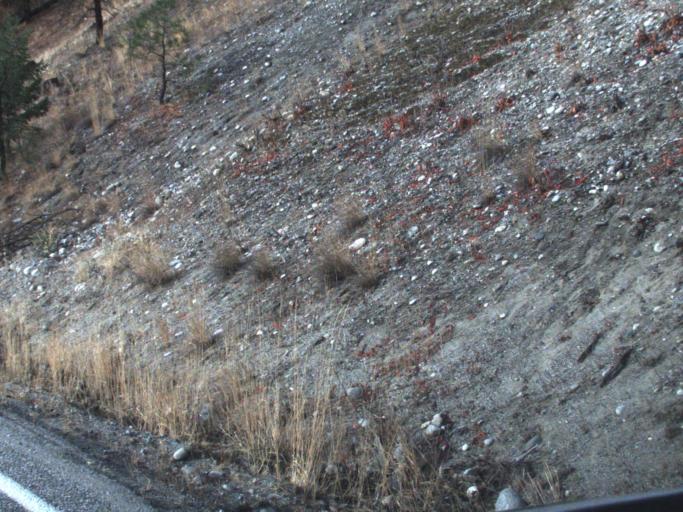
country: US
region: Washington
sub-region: Stevens County
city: Kettle Falls
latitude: 48.7952
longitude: -118.1614
